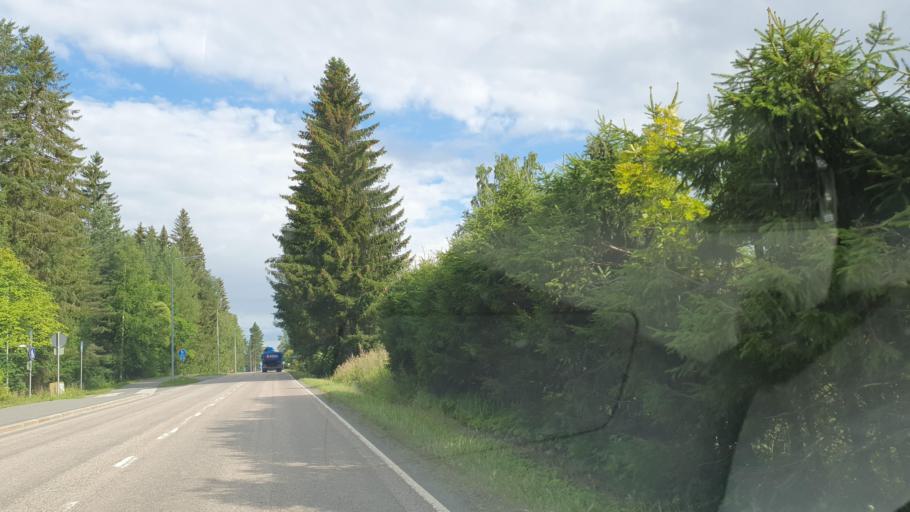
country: FI
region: Central Finland
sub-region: Jyvaeskylae
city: Jyvaeskylae
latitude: 62.1852
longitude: 25.7181
